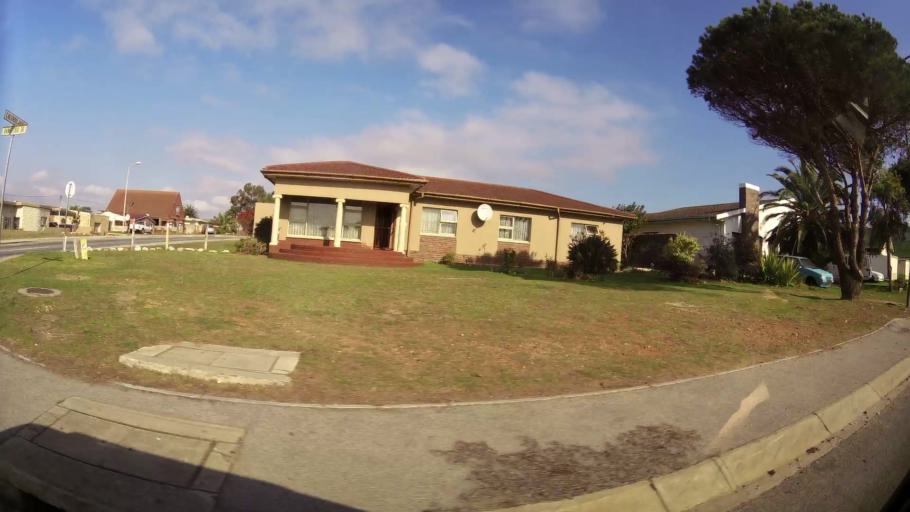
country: ZA
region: Eastern Cape
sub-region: Nelson Mandela Bay Metropolitan Municipality
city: Port Elizabeth
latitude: -33.9213
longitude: 25.5317
